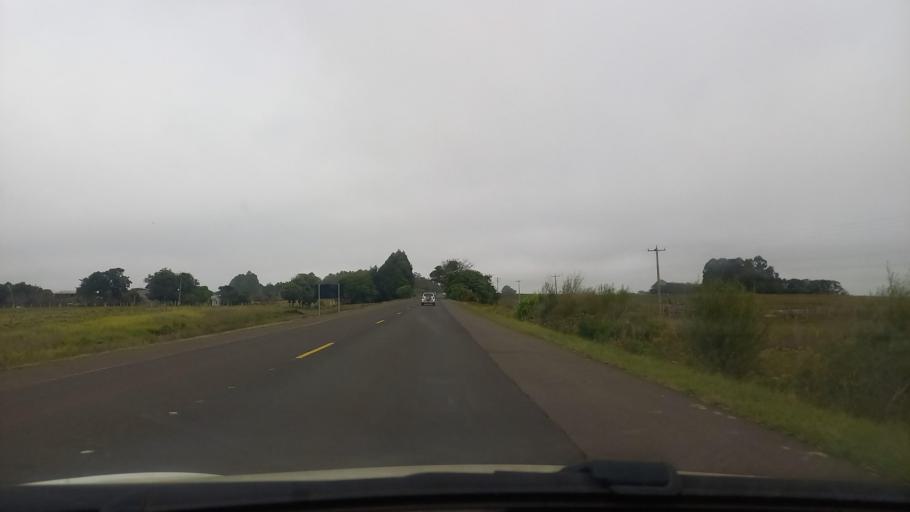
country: BR
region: Rio Grande do Sul
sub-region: Rosario Do Sul
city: Rosario do Sul
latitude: -30.3207
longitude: -55.0011
